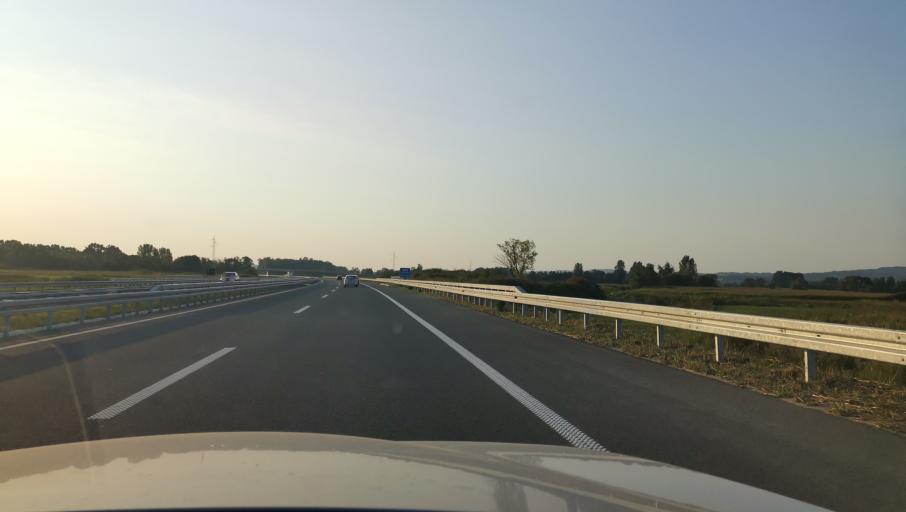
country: RS
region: Central Serbia
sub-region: Kolubarski Okrug
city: Ljig
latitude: 44.2800
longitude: 20.2608
